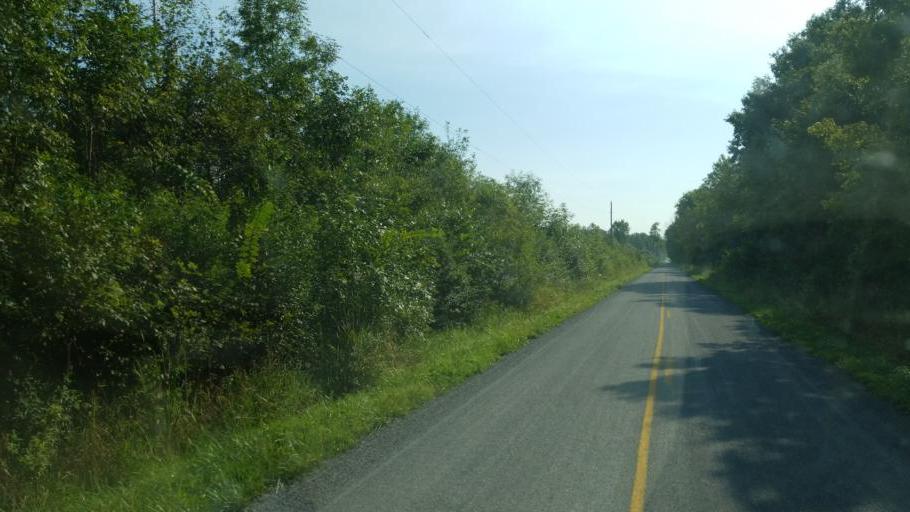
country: US
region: Ohio
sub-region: Ashtabula County
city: Orwell
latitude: 41.4754
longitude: -80.9033
